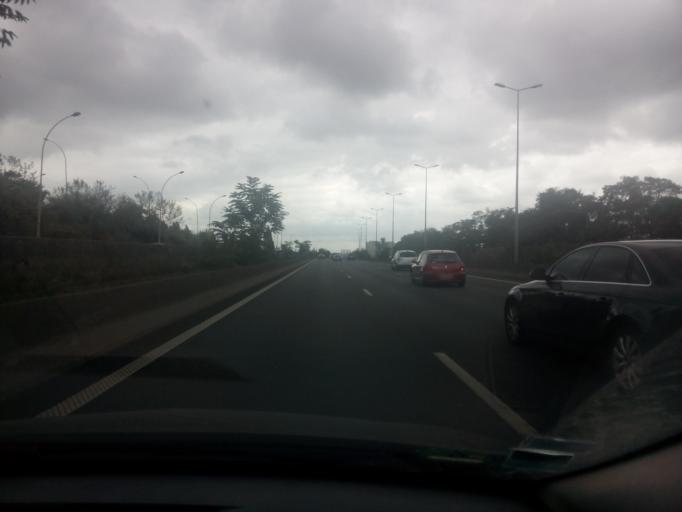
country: FR
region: Ile-de-France
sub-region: Departement du Val-de-Marne
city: L'Hay-les-Roses
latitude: 48.7873
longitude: 2.3451
